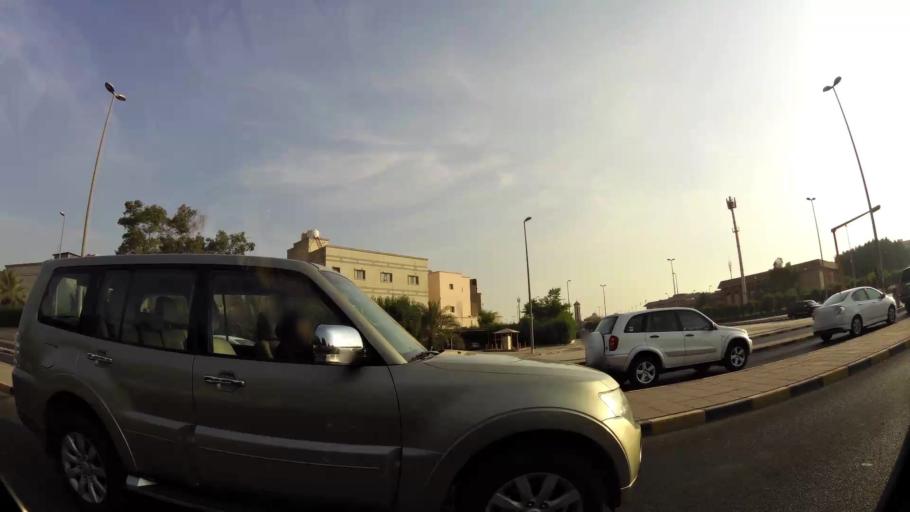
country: KW
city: Al Funaytis
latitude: 29.2218
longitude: 48.0752
